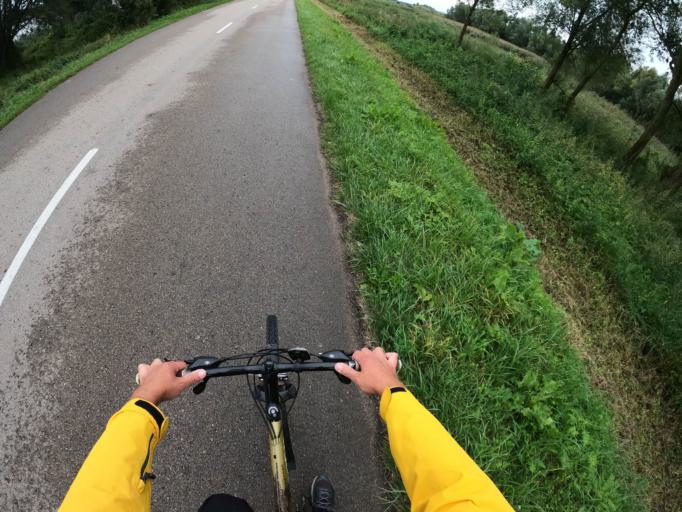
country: LT
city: Rusne
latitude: 55.3436
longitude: 21.3331
